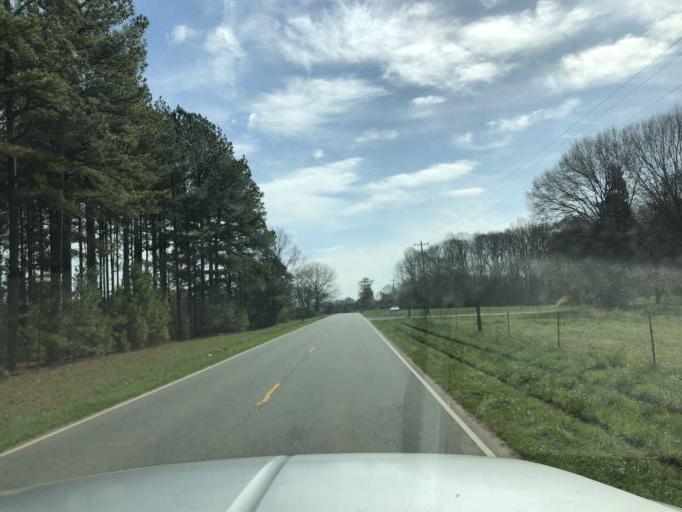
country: US
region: North Carolina
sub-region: Cleveland County
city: Shelby
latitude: 35.3798
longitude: -81.6126
